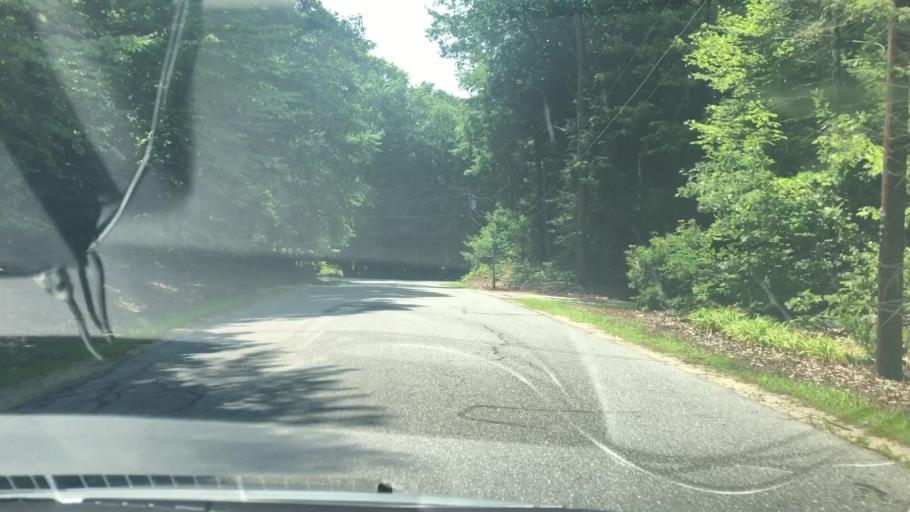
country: US
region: New Hampshire
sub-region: Hillsborough County
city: Milford
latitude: 42.8741
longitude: -71.6181
